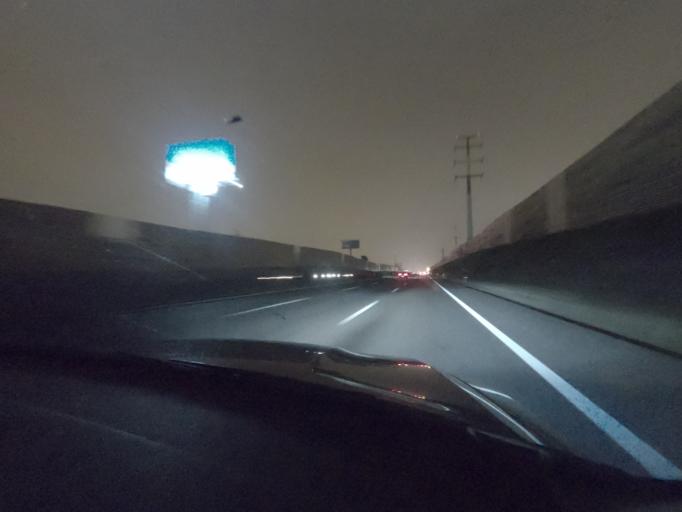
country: PT
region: Lisbon
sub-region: Loures
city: Sao Joao da Talha
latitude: 38.8277
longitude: -9.0982
